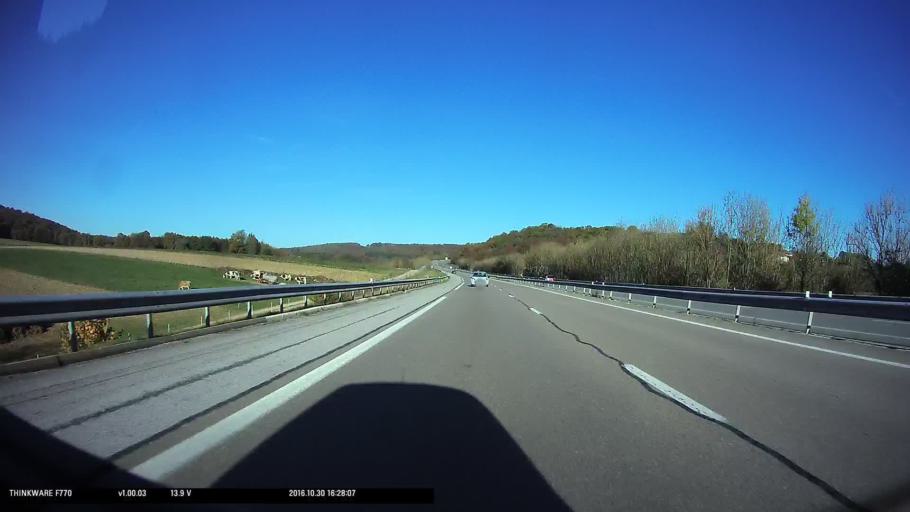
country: FR
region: Franche-Comte
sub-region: Departement du Doubs
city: Baume-les-Dames
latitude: 47.3433
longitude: 6.2974
